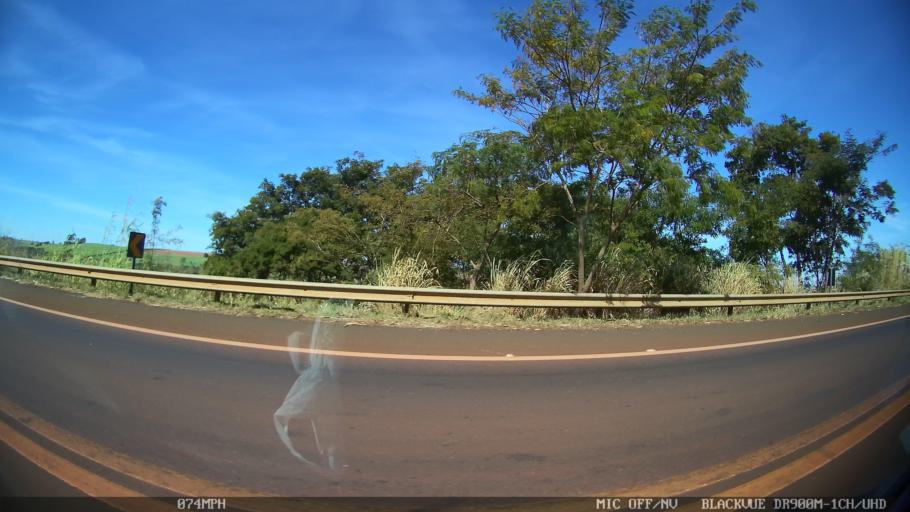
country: BR
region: Sao Paulo
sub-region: Sao Joaquim Da Barra
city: Sao Joaquim da Barra
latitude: -20.5612
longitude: -47.6861
